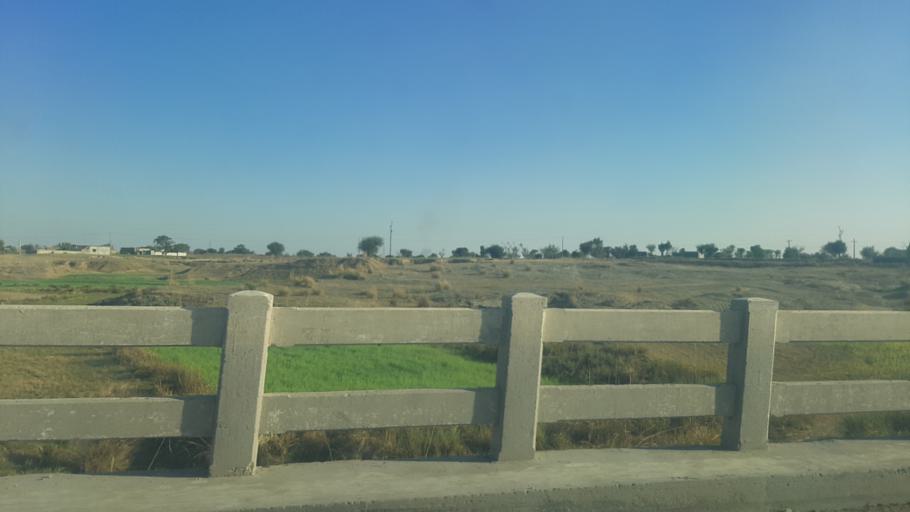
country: PK
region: Punjab
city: Talagang
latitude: 32.8898
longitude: 72.2227
